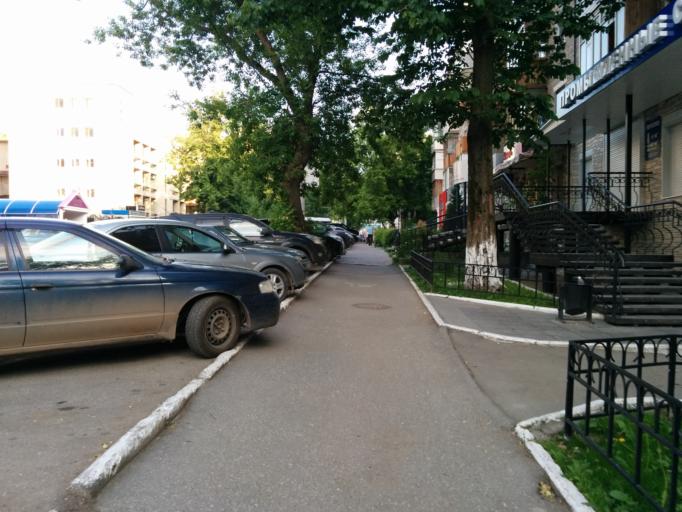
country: RU
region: Perm
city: Perm
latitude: 58.0072
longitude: 56.2481
